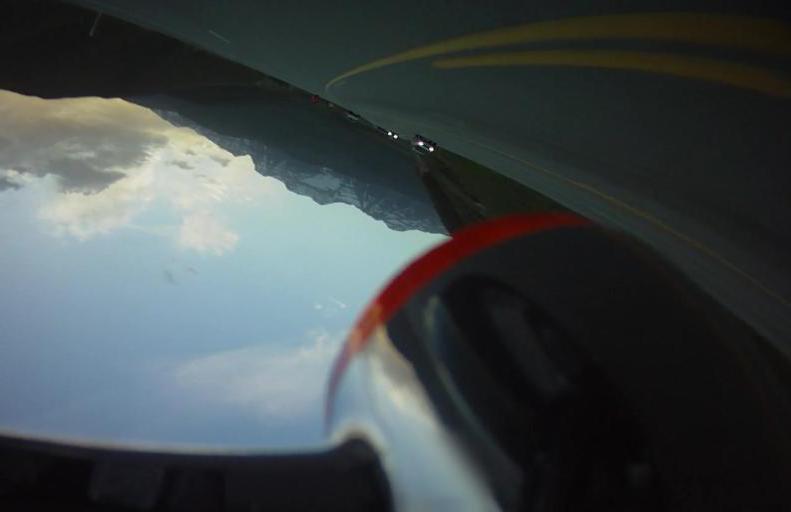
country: US
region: Utah
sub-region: Wasatch County
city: Midway
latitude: 40.4114
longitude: -111.5112
